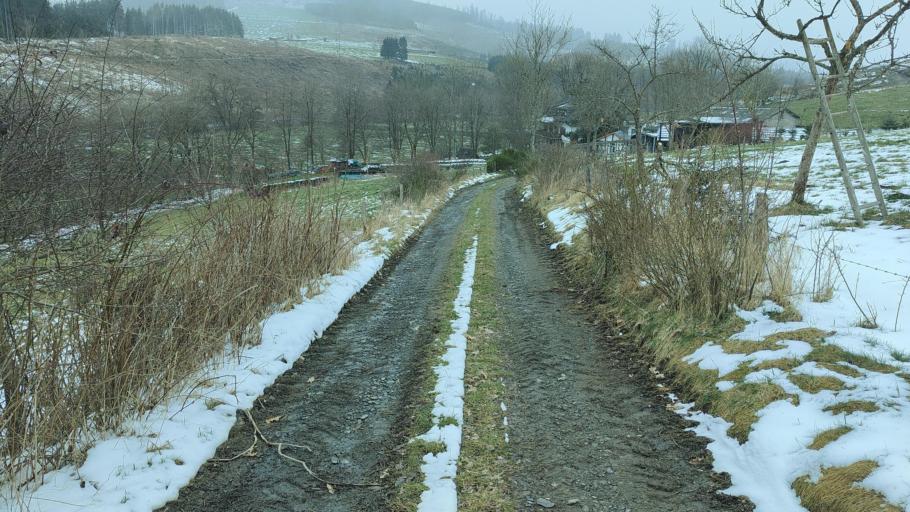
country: DE
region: North Rhine-Westphalia
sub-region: Regierungsbezirk Arnsberg
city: Bad Berleburg
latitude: 51.0859
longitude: 8.4282
